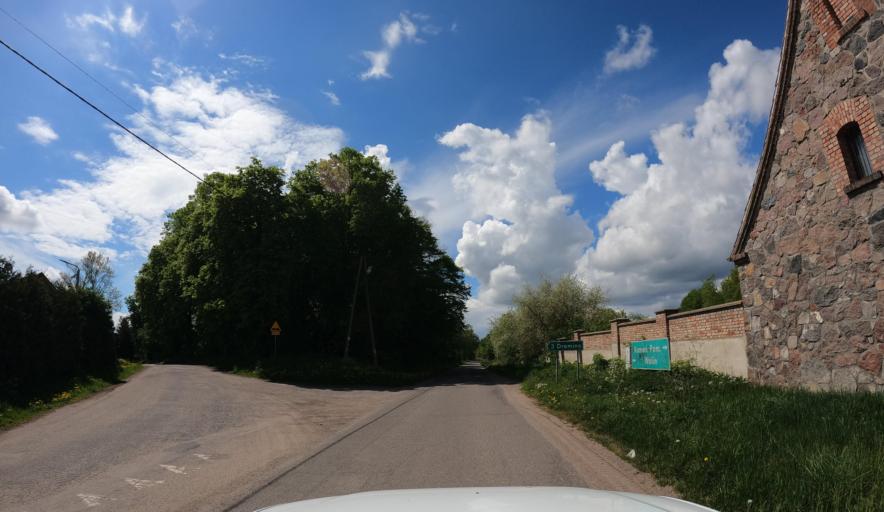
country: PL
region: West Pomeranian Voivodeship
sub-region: Powiat kamienski
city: Wolin
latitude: 53.9040
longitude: 14.6749
